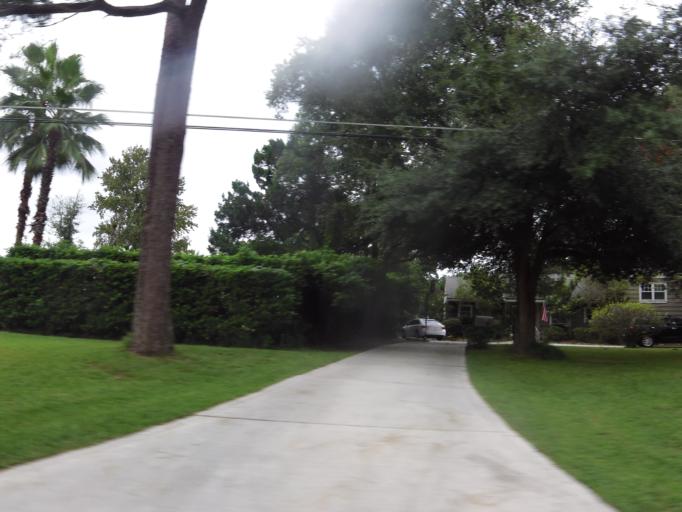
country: US
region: Florida
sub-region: Clay County
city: Bellair-Meadowbrook Terrace
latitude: 30.2494
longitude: -81.7058
